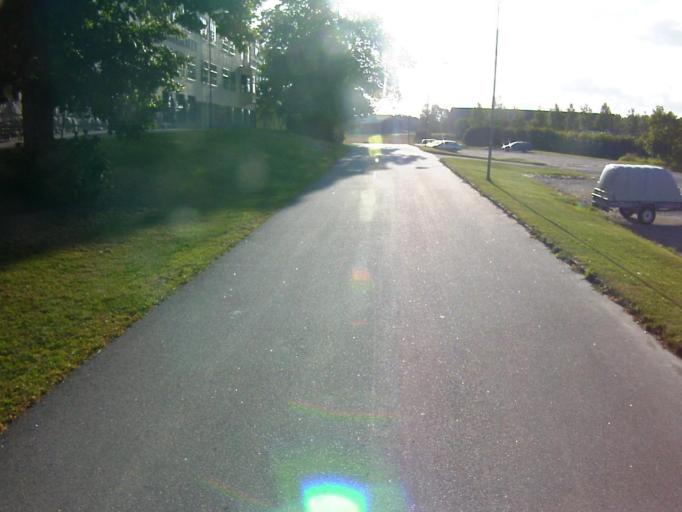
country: SE
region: Soedermanland
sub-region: Eskilstuna Kommun
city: Eskilstuna
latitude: 59.3781
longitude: 16.5412
